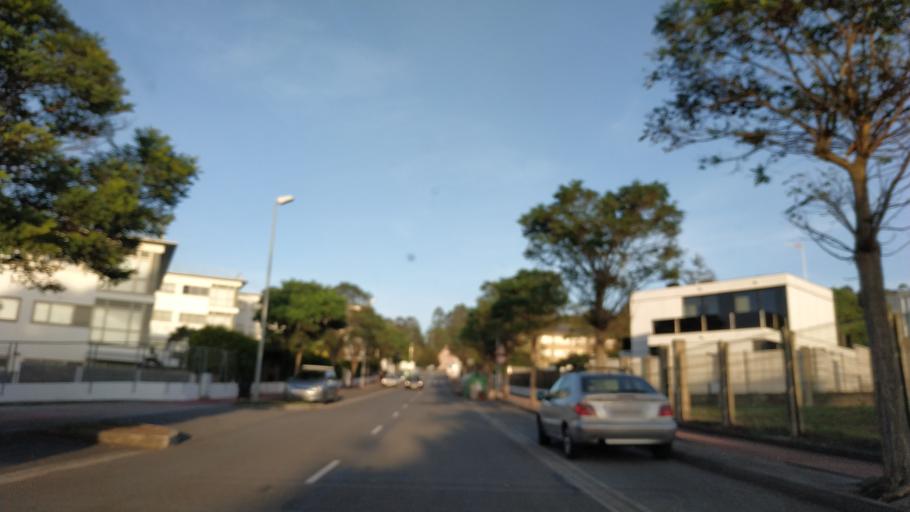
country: ES
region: Galicia
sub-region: Provincia da Coruna
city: Oleiros
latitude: 43.3701
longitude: -8.3372
